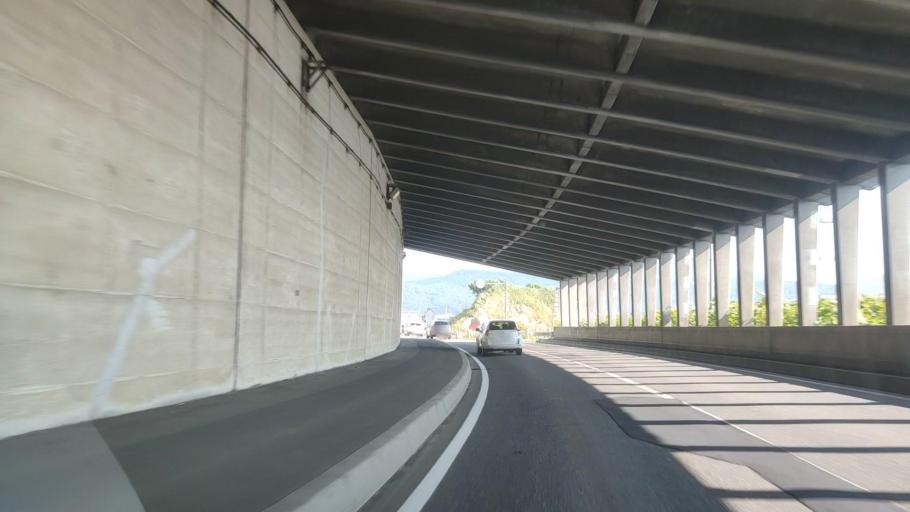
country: JP
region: Hokkaido
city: Ishikari
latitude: 43.5921
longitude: 141.3849
